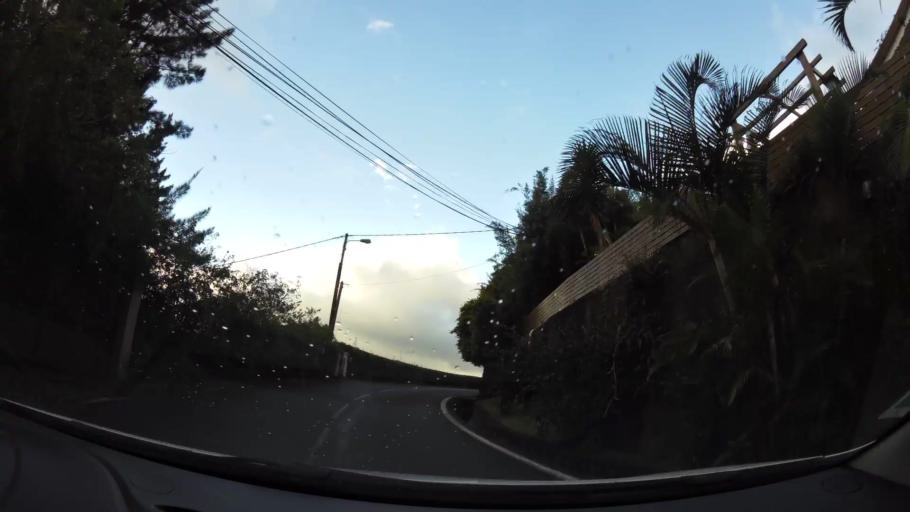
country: RE
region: Reunion
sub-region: Reunion
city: Saint-Denis
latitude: -20.9186
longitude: 55.4379
